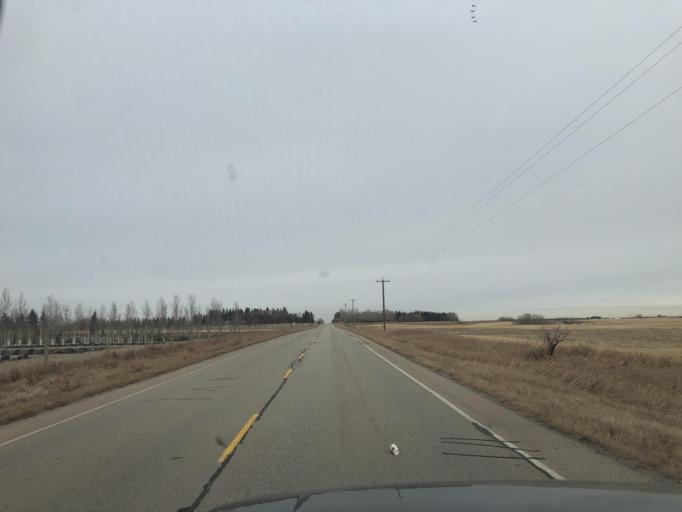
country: CA
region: Alberta
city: Chestermere
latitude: 50.9845
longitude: -113.8654
